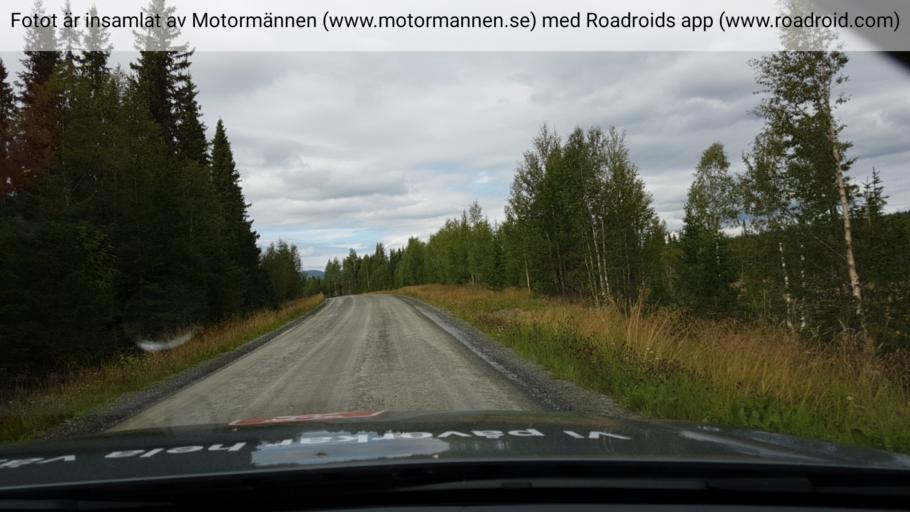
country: SE
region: Jaemtland
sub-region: Krokoms Kommun
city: Valla
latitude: 63.6902
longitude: 13.6723
